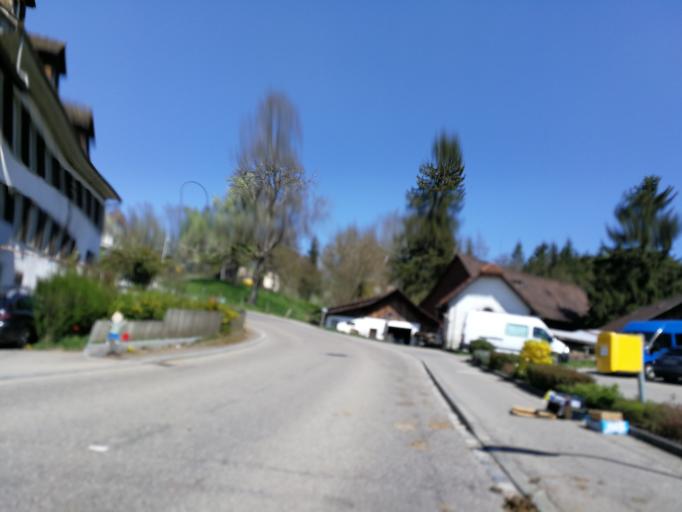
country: CH
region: Zurich
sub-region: Bezirk Meilen
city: Herrliberg
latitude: 47.2946
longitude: 8.6315
